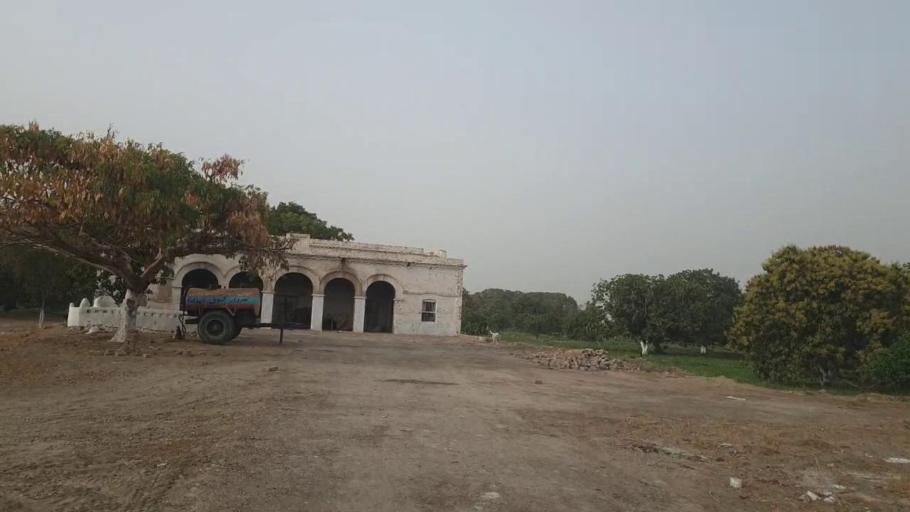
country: PK
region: Sindh
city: Kunri
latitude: 25.0679
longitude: 69.4418
